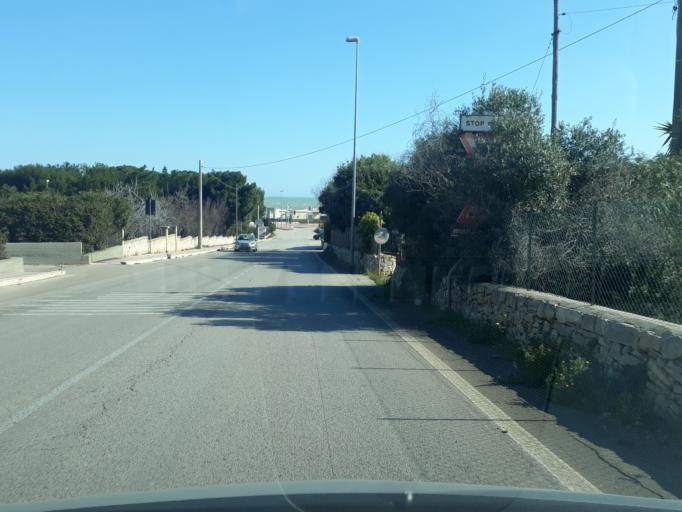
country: IT
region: Apulia
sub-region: Provincia di Brindisi
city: Fasano
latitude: 40.9039
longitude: 17.3484
